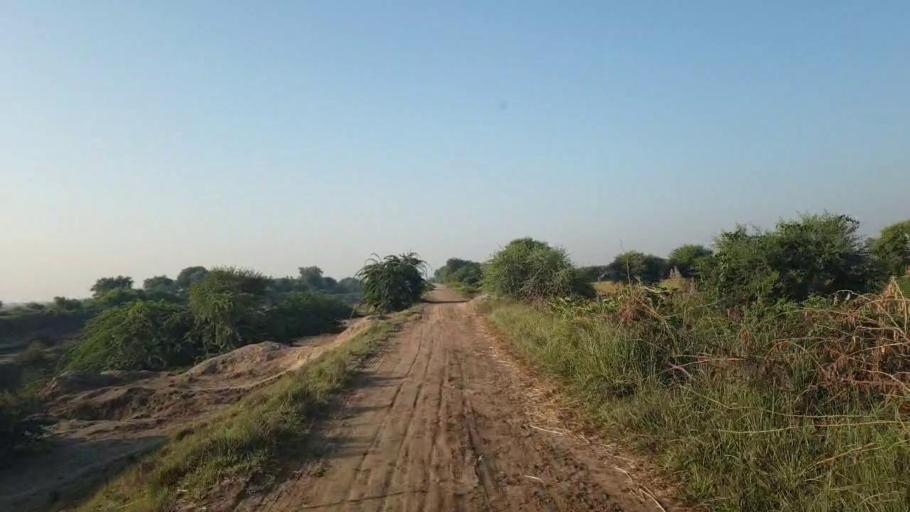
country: PK
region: Sindh
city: Badin
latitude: 24.6195
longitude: 68.7892
